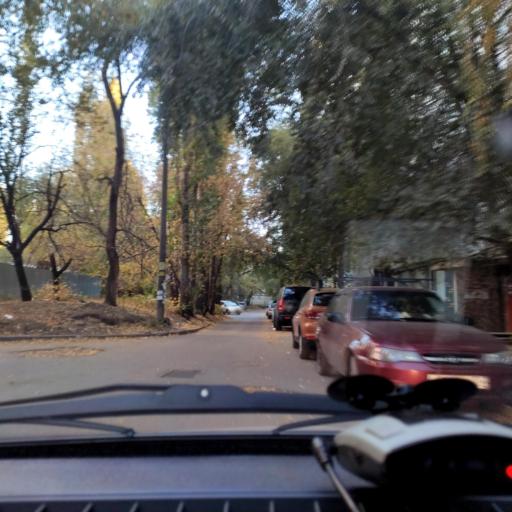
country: RU
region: Voronezj
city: Voronezh
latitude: 51.6854
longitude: 39.1947
